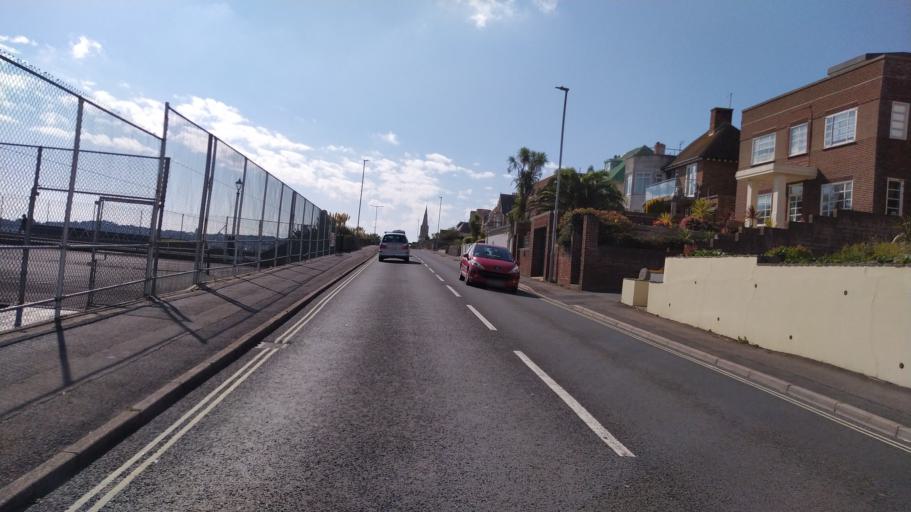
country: GB
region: England
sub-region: Dorset
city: Weymouth
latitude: 50.6224
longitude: -2.4470
